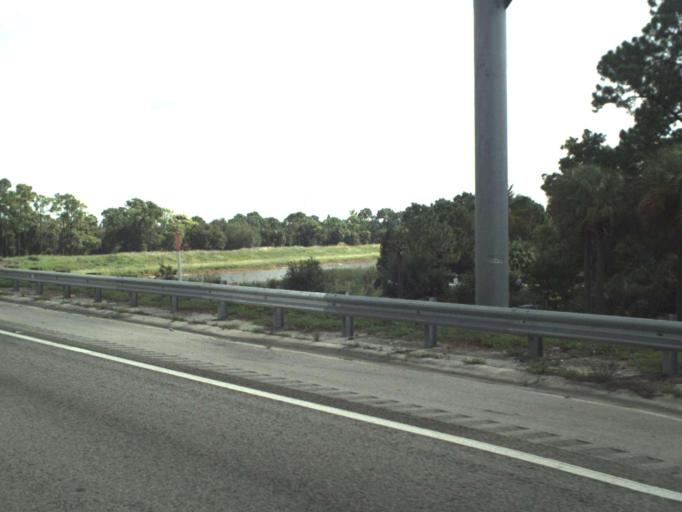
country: US
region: Florida
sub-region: Palm Beach County
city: Limestone Creek
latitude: 26.9291
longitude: -80.1484
